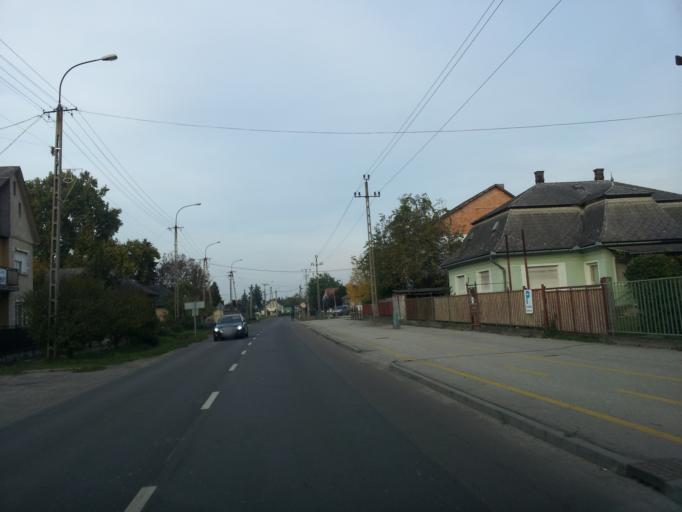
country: HU
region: Pest
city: Nagykata
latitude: 47.4133
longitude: 19.7490
